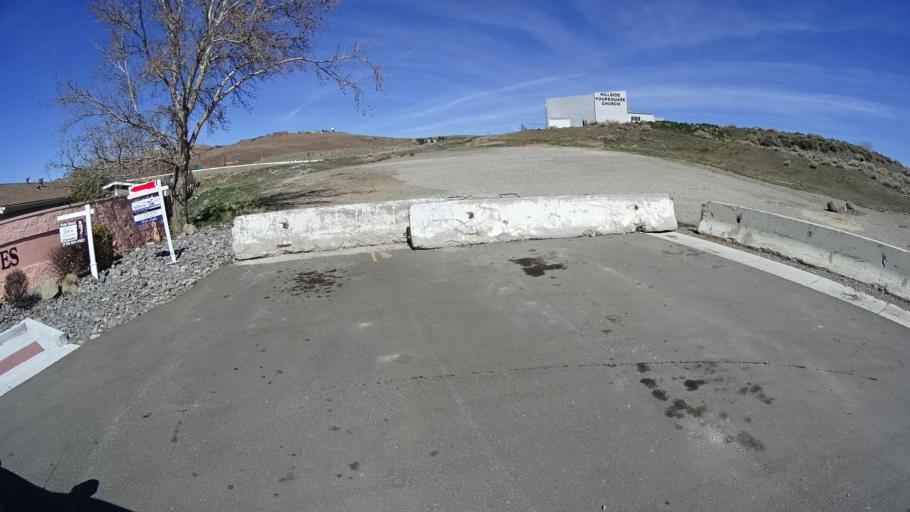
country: US
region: Nevada
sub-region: Washoe County
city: Reno
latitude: 39.5604
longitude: -119.7985
